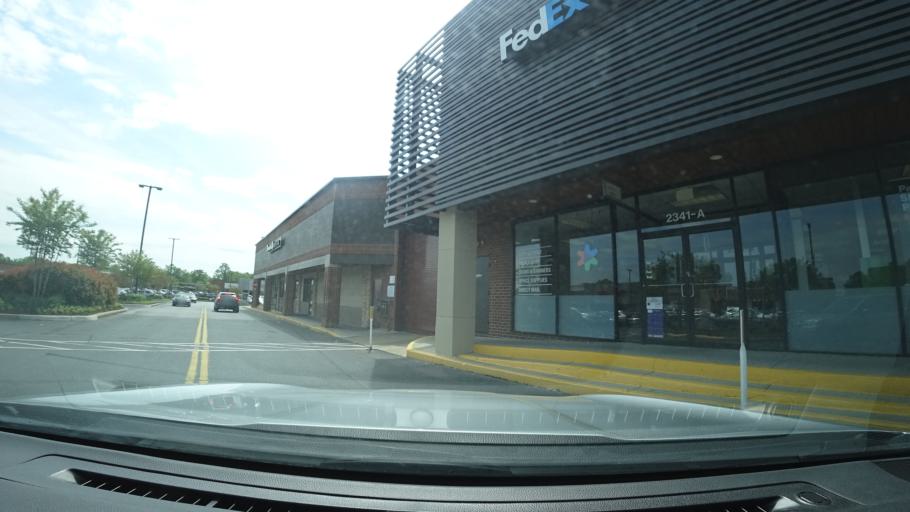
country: US
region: Maryland
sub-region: Anne Arundel County
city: Parole
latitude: 38.9798
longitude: -76.5446
